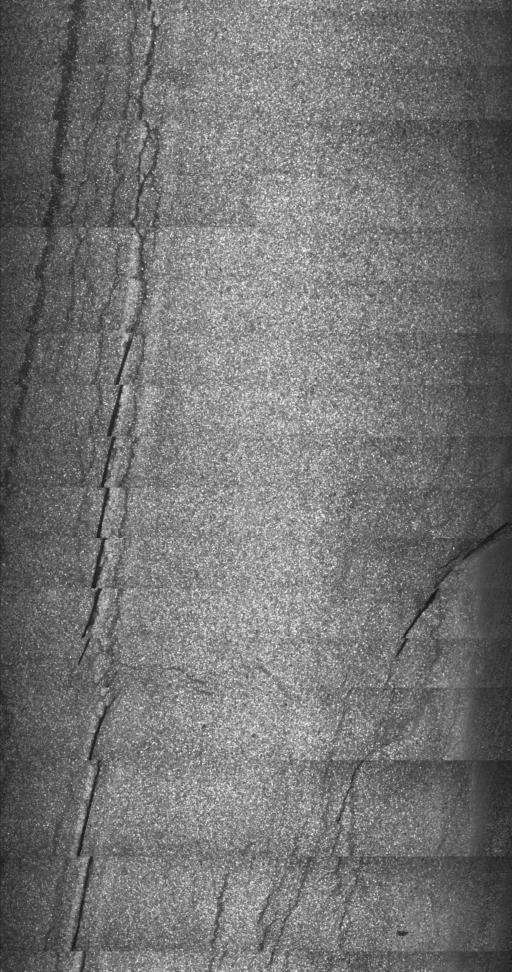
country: US
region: Vermont
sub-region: Bennington County
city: Manchester Center
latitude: 43.1945
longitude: -72.9955
